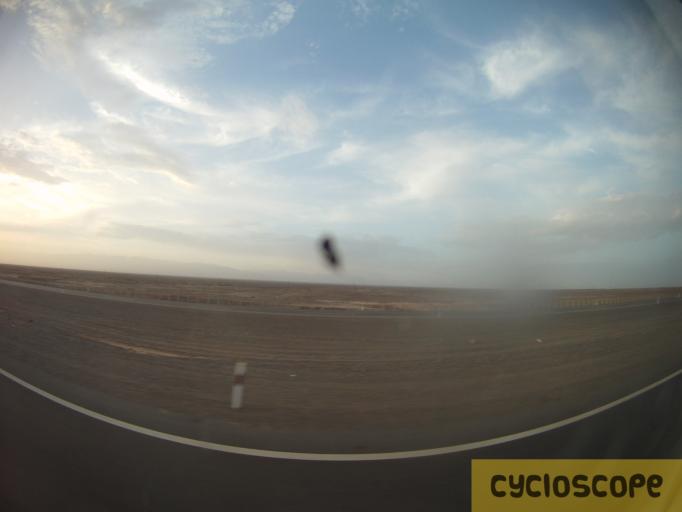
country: CN
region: Xinjiang Uygur Zizhiqu
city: Shanshan
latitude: 42.9012
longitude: 89.8358
